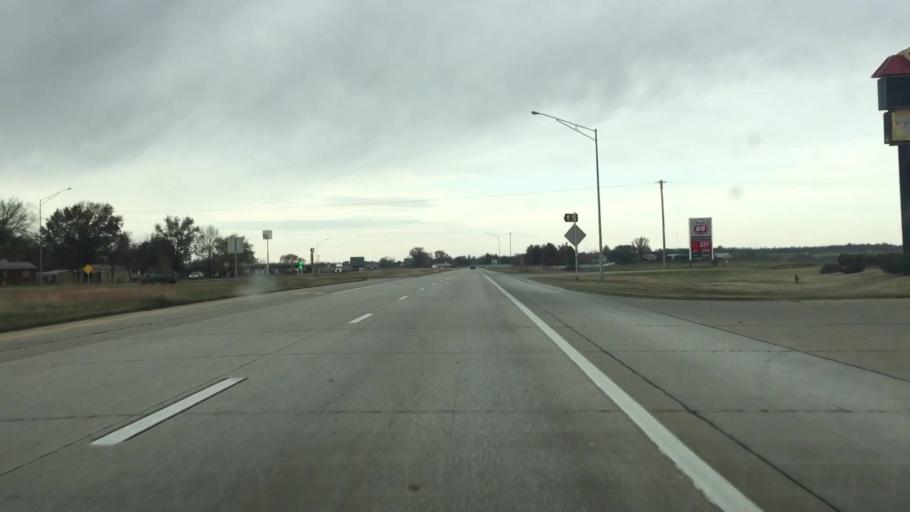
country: US
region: Missouri
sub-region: Saint Clair County
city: Osceola
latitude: 38.1398
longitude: -93.7175
